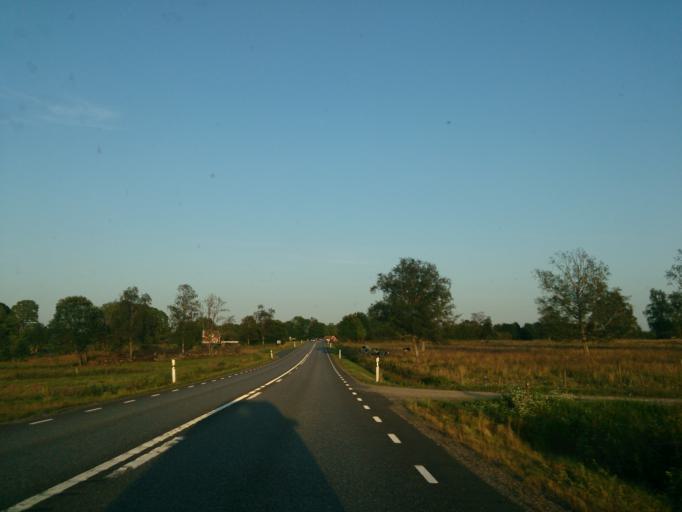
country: SE
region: Joenkoeping
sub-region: Varnamo Kommun
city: Rydaholm
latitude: 56.9981
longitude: 14.2834
